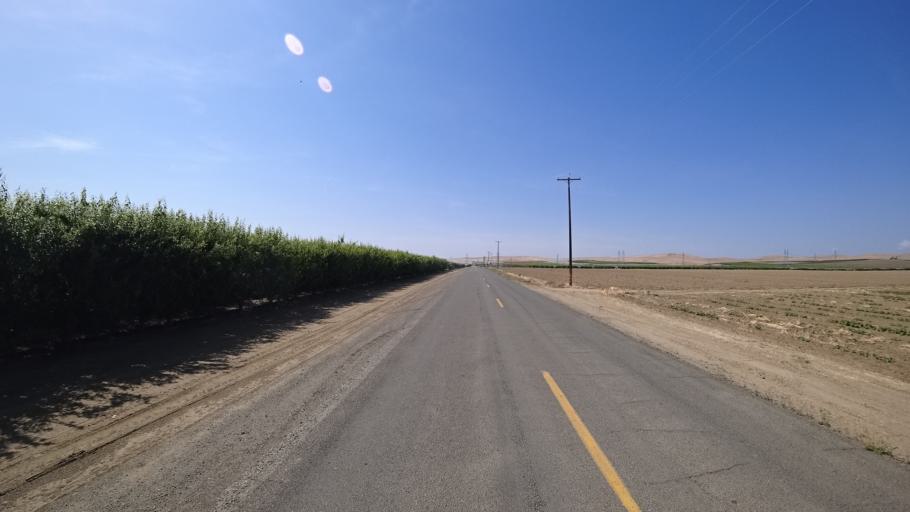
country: US
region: California
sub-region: Kings County
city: Kettleman City
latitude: 36.0397
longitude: -120.0036
